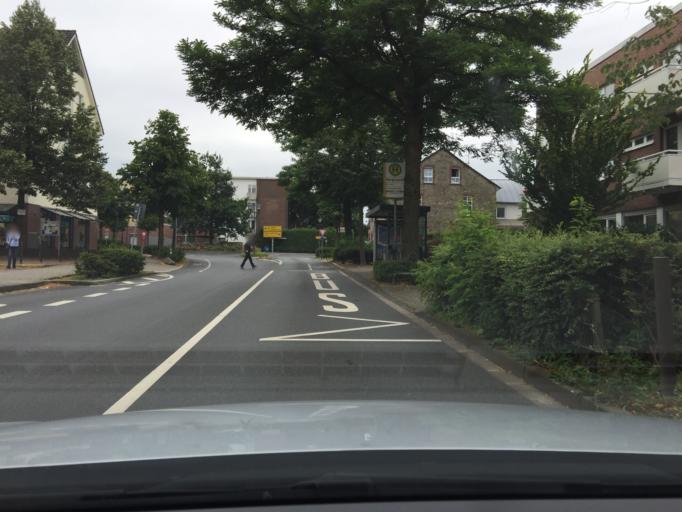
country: DE
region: North Rhine-Westphalia
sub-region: Regierungsbezirk Dusseldorf
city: Heiligenhaus
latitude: 51.3305
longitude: 6.9087
